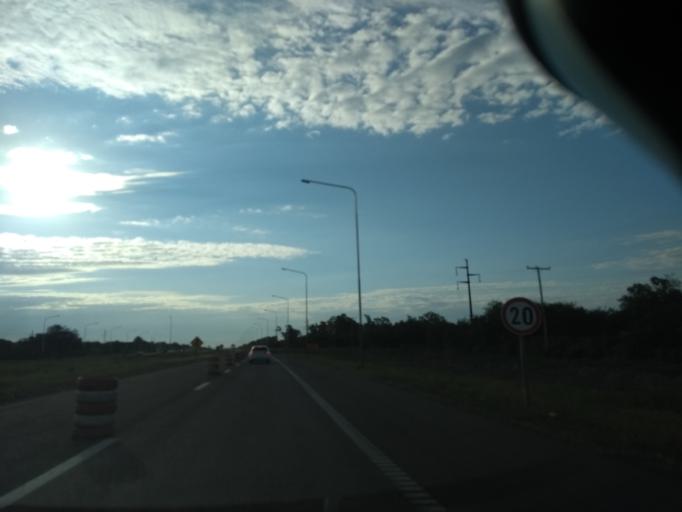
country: AR
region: Chaco
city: Puerto Tirol
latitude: -27.2715
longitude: -59.1428
